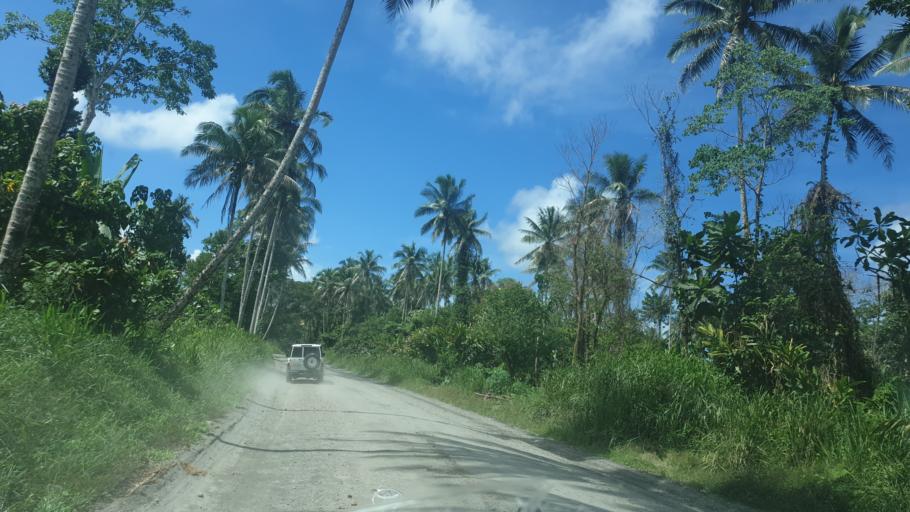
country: PG
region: Bougainville
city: Panguna
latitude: -6.7389
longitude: 155.6705
